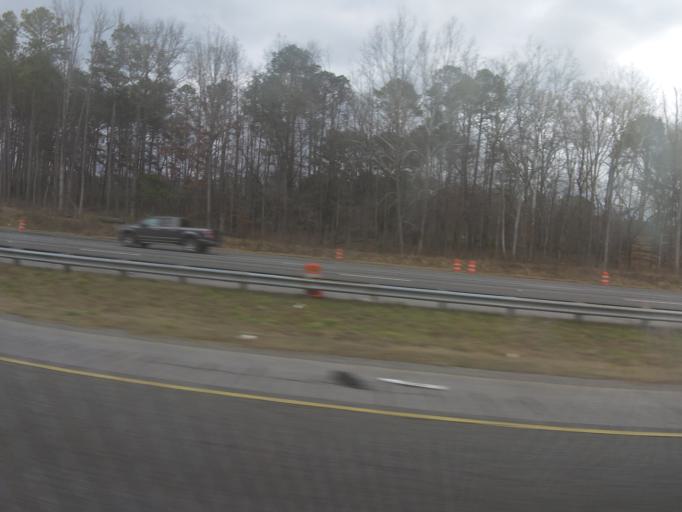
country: US
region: Georgia
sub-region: Whitfield County
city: Dalton
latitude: 34.6498
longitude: -84.9826
